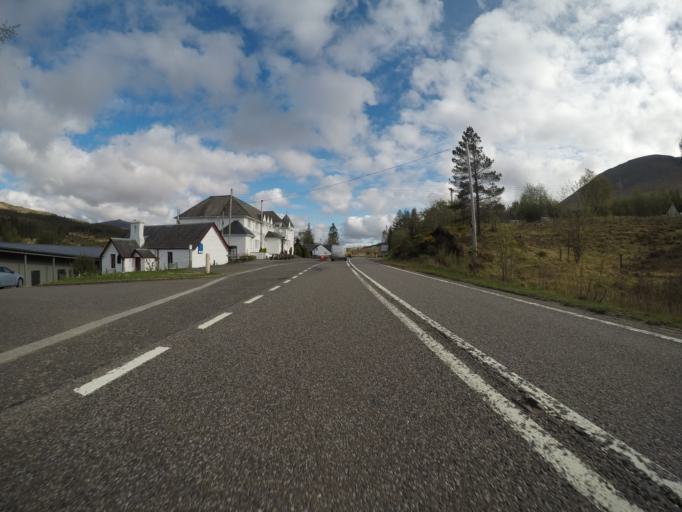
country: GB
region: Scotland
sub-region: Highland
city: Spean Bridge
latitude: 56.5173
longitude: -4.7688
